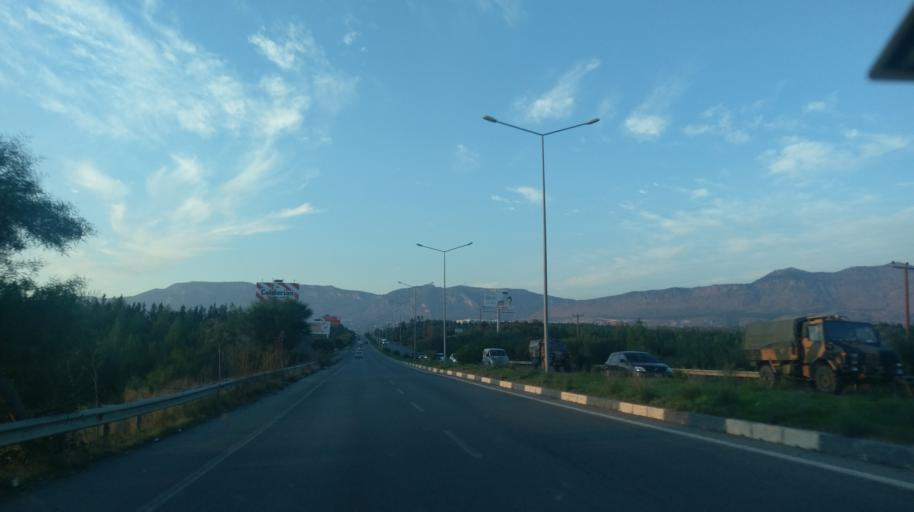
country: CY
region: Lefkosia
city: Nicosia
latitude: 35.2443
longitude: 33.3080
